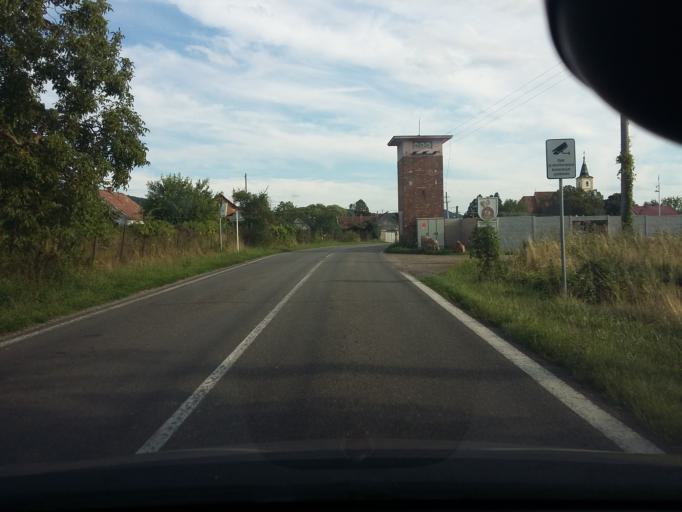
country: SK
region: Bratislavsky
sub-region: Okres Malacky
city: Malacky
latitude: 48.4083
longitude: 17.1562
